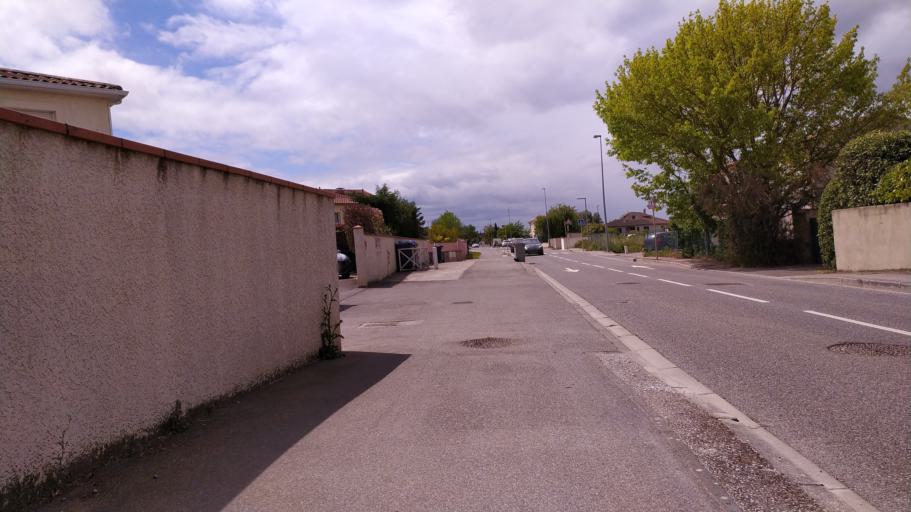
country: FR
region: Midi-Pyrenees
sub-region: Departement de la Haute-Garonne
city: Plaisance-du-Touch
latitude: 43.5815
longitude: 1.2940
